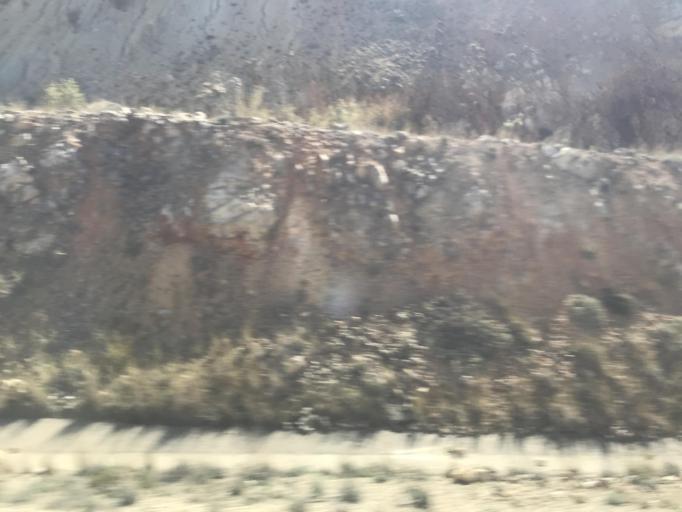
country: ES
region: Castille-La Mancha
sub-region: Provincia de Guadalajara
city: Anguita
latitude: 41.0847
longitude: -2.4067
